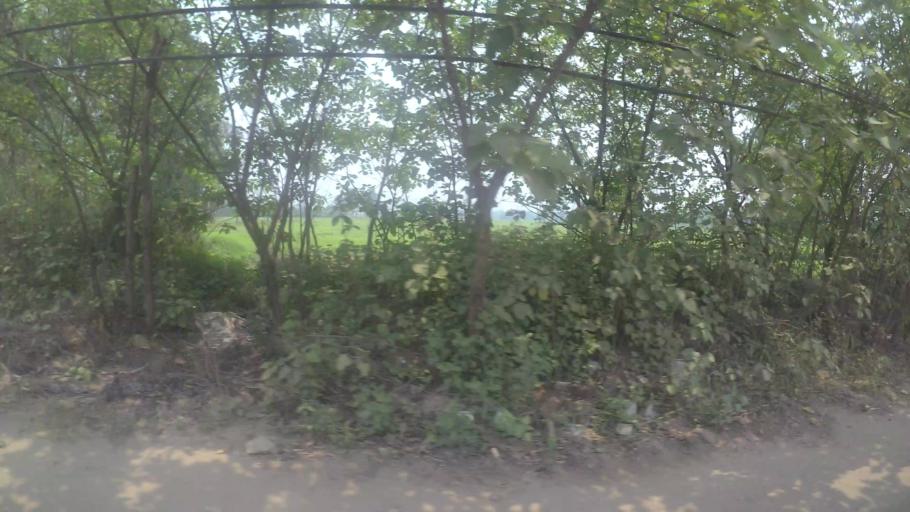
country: VN
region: Ha Noi
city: Thanh Xuan
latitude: 21.0032
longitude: 105.7675
